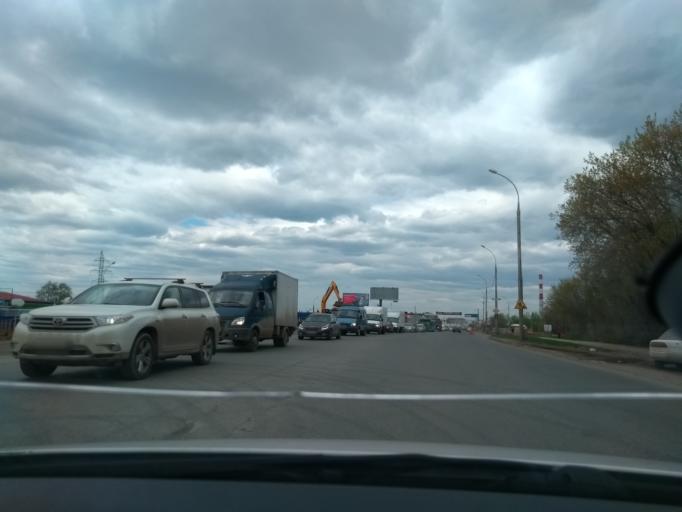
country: RU
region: Perm
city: Froly
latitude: 57.9492
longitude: 56.2652
